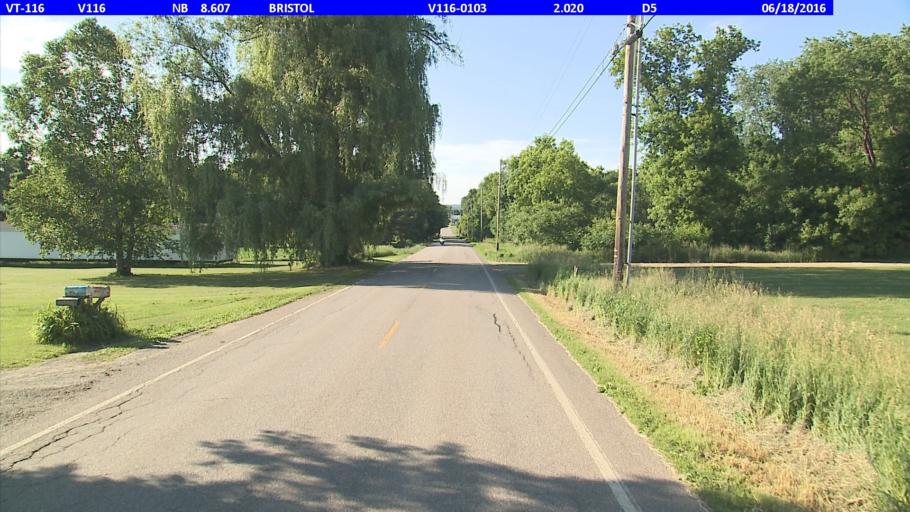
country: US
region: Vermont
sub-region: Addison County
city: Bristol
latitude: 44.0827
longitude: -73.0881
